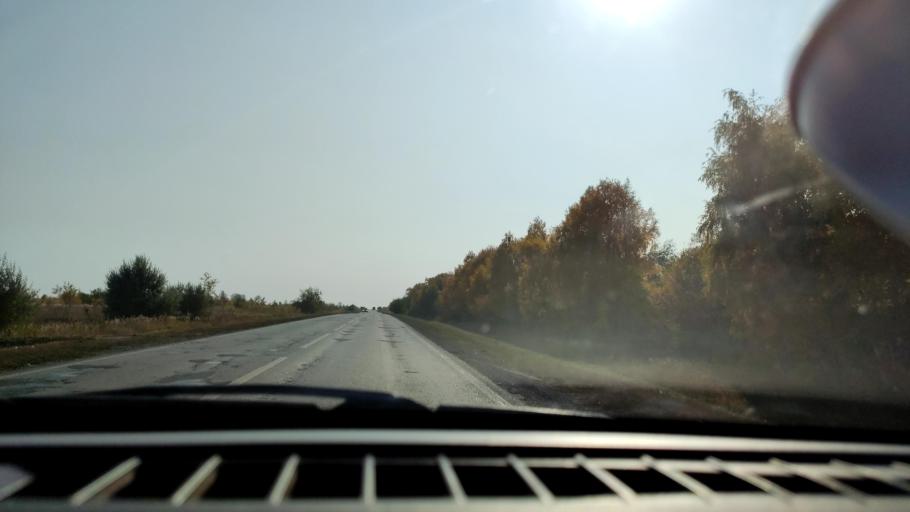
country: RU
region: Samara
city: Smyshlyayevka
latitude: 53.1344
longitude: 50.3718
